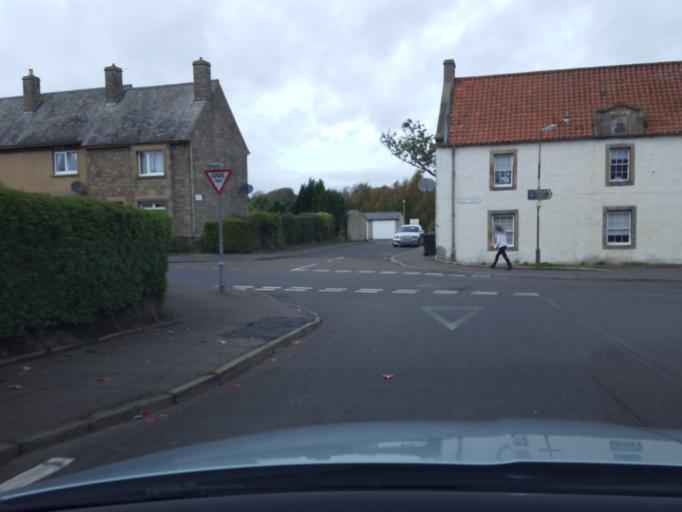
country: GB
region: Scotland
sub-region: Edinburgh
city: Ratho
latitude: 55.9215
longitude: -3.3802
